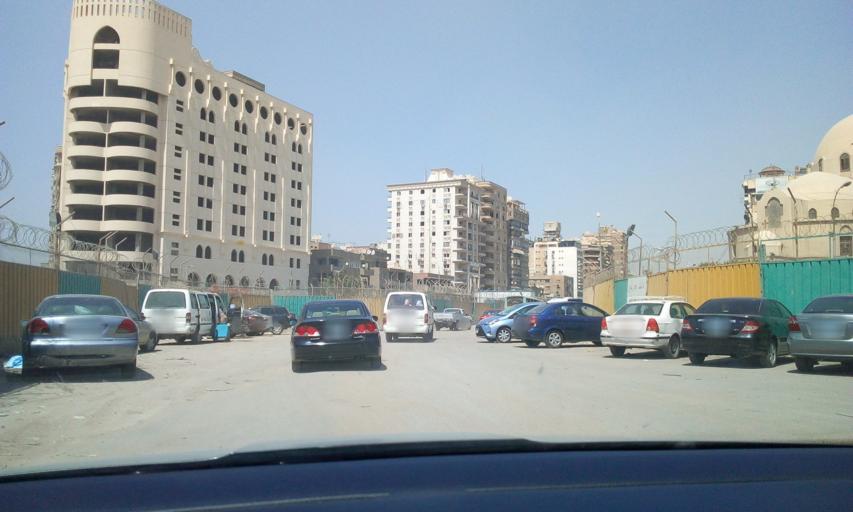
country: EG
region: Muhafazat al Qahirah
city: Cairo
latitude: 30.1077
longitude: 31.3385
